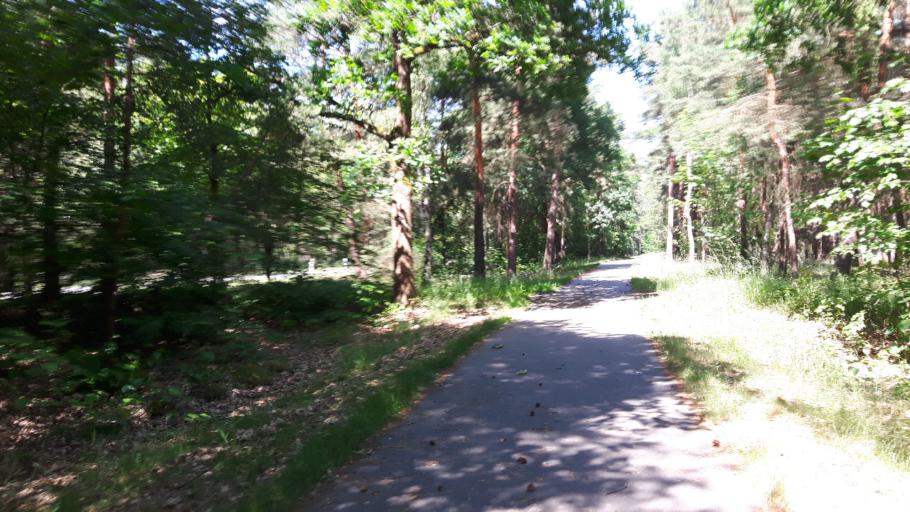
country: DE
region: Brandenburg
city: Treuenbrietzen
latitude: 52.0522
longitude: 12.8188
